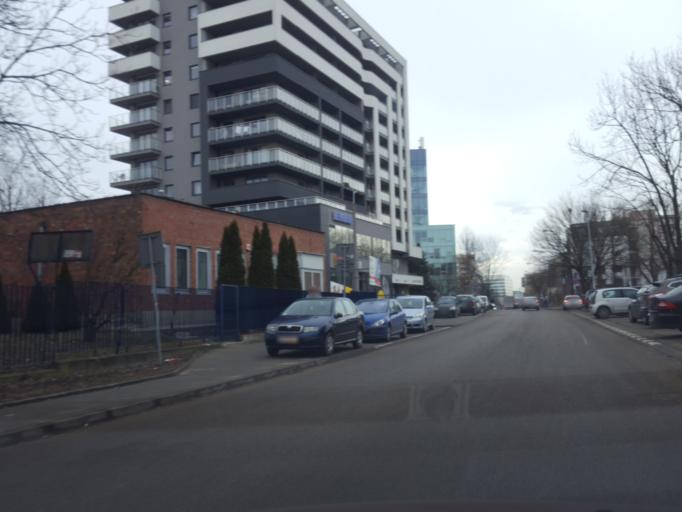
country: PL
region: Lesser Poland Voivodeship
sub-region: Krakow
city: Krakow
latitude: 50.0570
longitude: 19.9639
